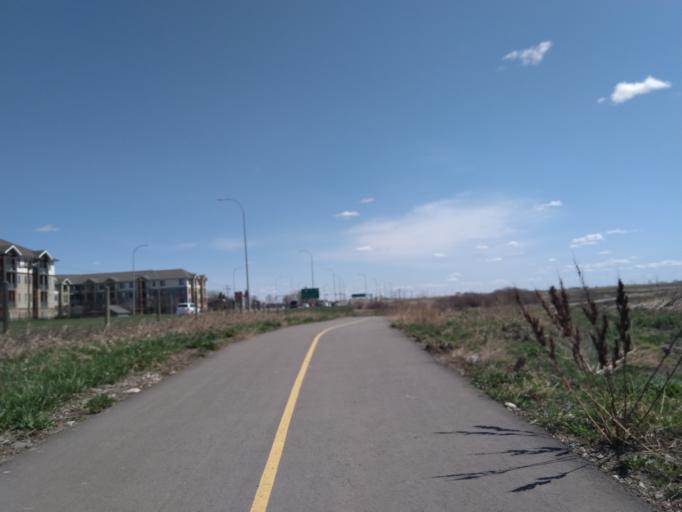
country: CA
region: Alberta
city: Chestermere
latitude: 51.0375
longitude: -113.9340
